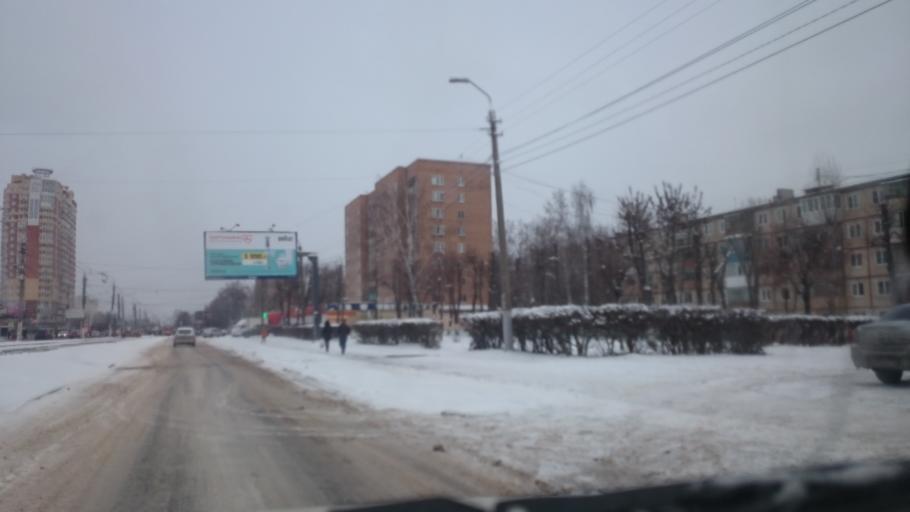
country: RU
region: Tula
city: Mendeleyevskiy
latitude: 54.1518
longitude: 37.5842
